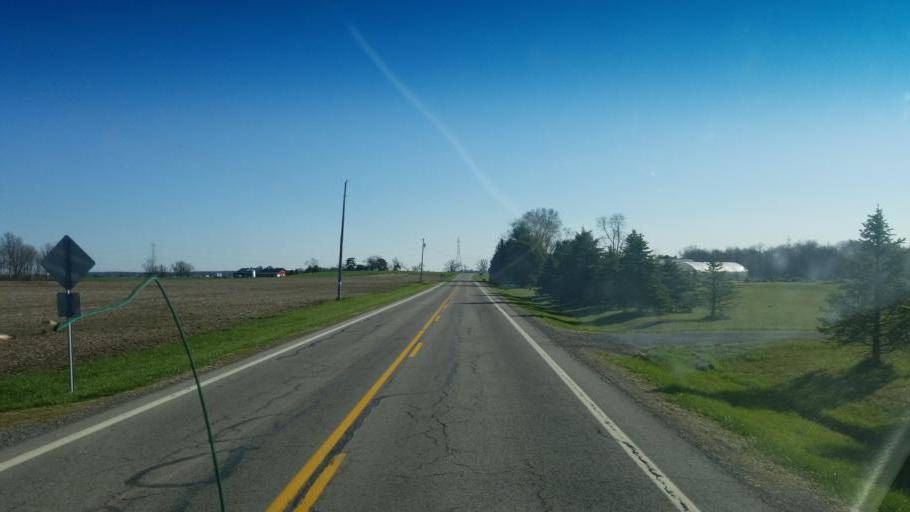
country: US
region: Ohio
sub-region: Logan County
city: Northwood
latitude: 40.5160
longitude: -83.6375
